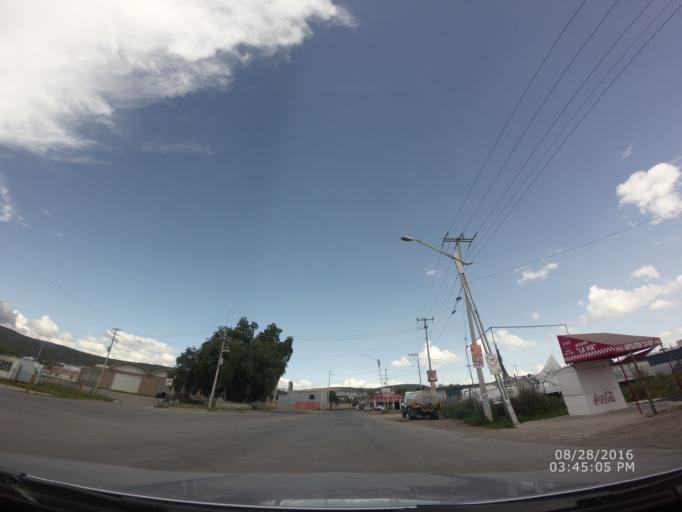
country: MX
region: Hidalgo
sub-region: Mineral de la Reforma
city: PRI Chacon
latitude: 20.0816
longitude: -98.7484
